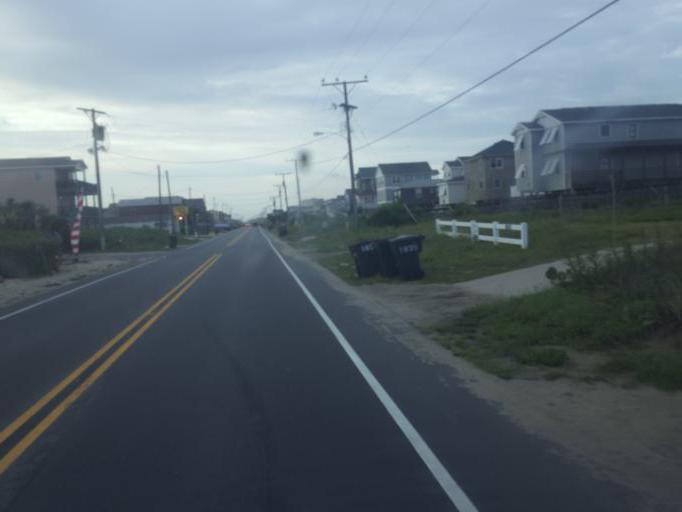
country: US
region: North Carolina
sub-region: Dare County
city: Kill Devil Hills
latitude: 36.0367
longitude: -75.6708
